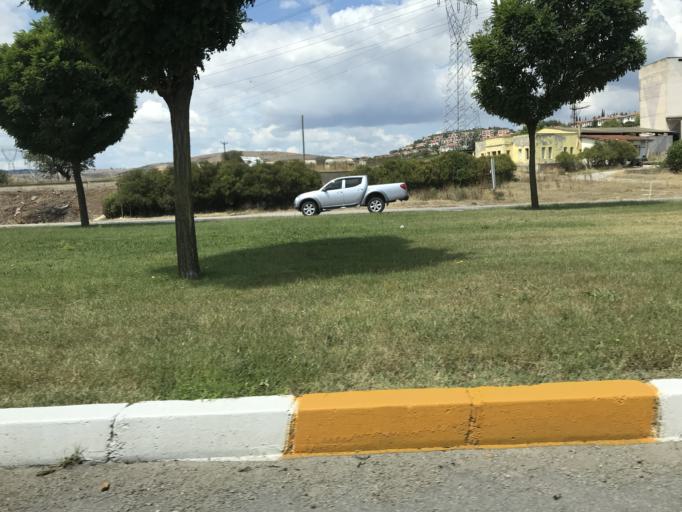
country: TR
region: Balikesir
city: Balikesir
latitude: 39.6949
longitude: 27.9620
